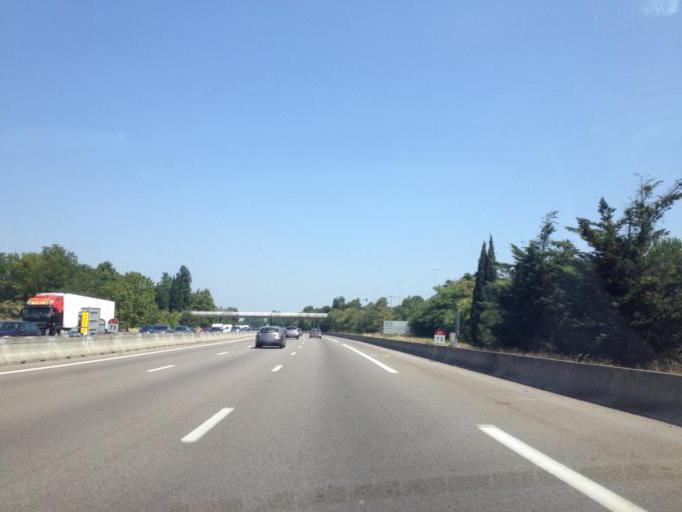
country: FR
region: Rhone-Alpes
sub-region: Departement de l'Ardeche
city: Guilherand-Granges
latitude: 44.9108
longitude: 4.8774
